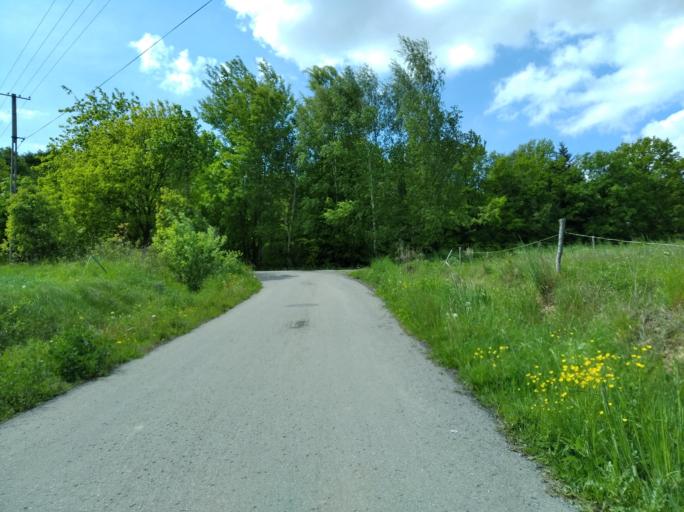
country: PL
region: Subcarpathian Voivodeship
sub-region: Powiat ropczycko-sedziszowski
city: Wielopole Skrzynskie
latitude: 49.9221
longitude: 21.6192
